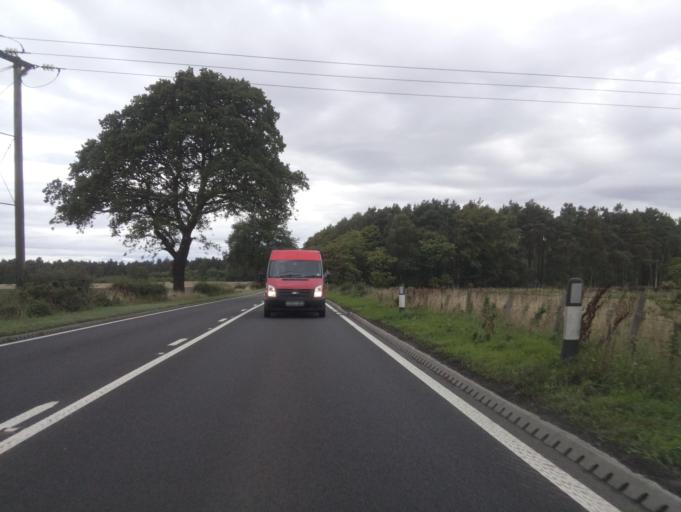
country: GB
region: Scotland
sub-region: Fife
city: High Valleyfield
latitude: 56.0663
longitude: -3.6452
